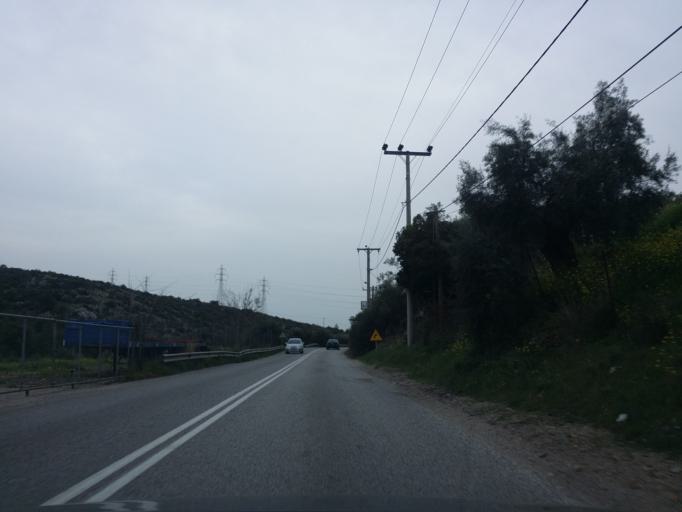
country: GR
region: Attica
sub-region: Nomarchia Dytikis Attikis
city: Mandra
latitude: 38.0890
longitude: 23.4780
